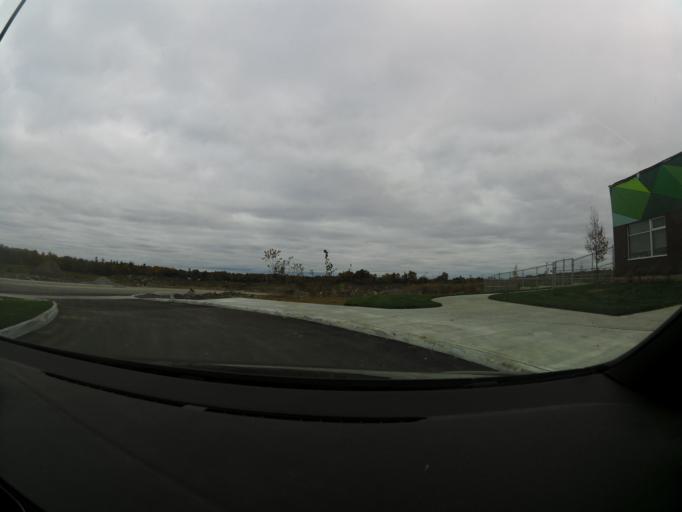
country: CA
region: Ontario
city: Bells Corners
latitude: 45.3367
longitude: -75.9402
